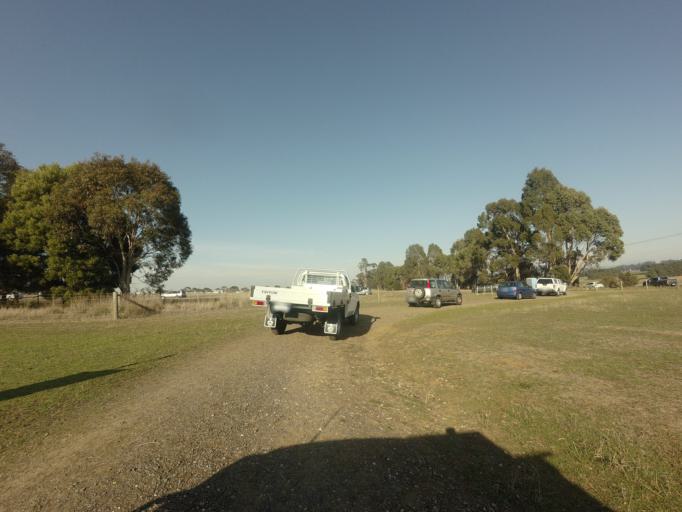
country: AU
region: Tasmania
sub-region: Northern Midlands
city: Longford
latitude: -41.5621
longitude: 146.9823
